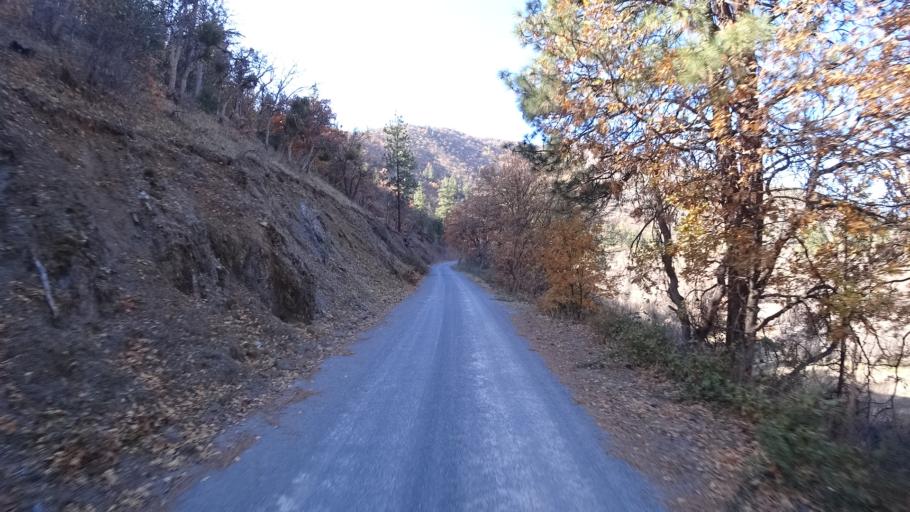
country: US
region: California
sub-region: Siskiyou County
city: Yreka
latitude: 41.8407
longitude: -122.6779
